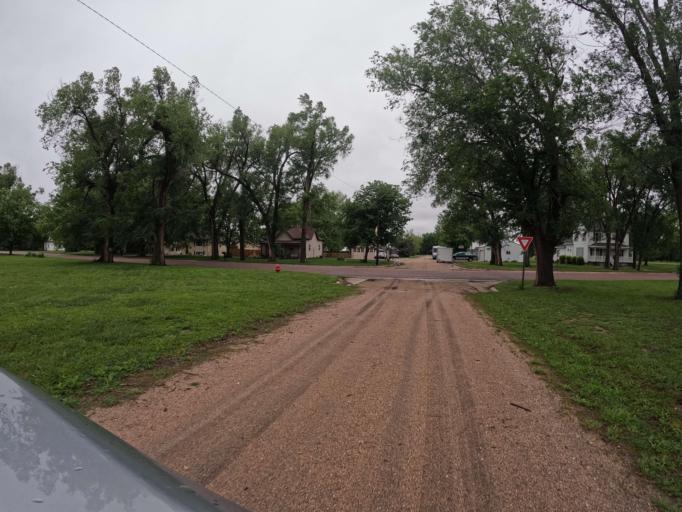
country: US
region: Nebraska
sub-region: Clay County
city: Harvard
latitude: 40.6254
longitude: -98.0967
